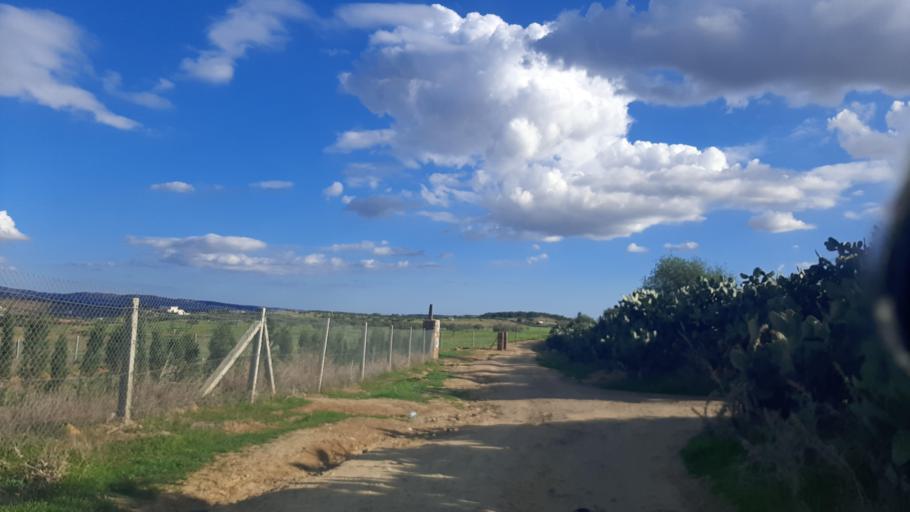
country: TN
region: Nabul
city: Bu `Urqub
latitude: 36.4650
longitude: 10.4827
